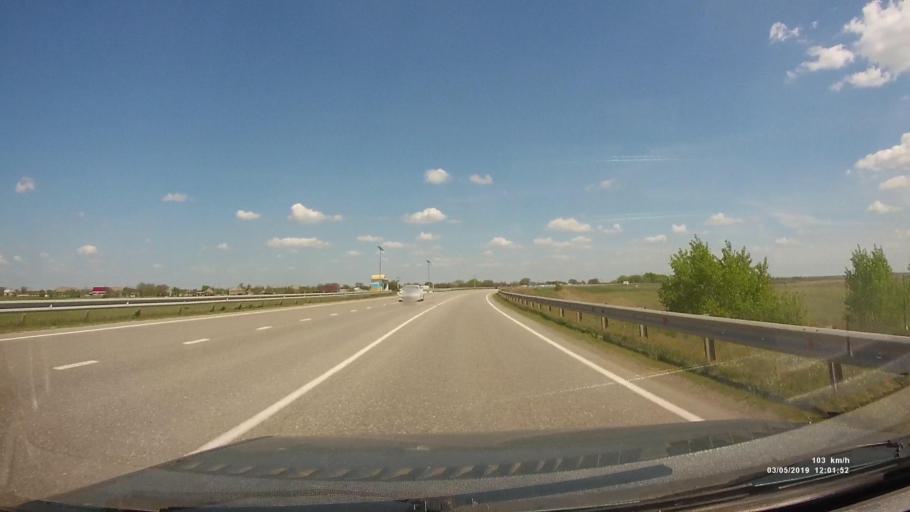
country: RU
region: Rostov
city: Bagayevskaya
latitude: 47.2687
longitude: 40.3557
